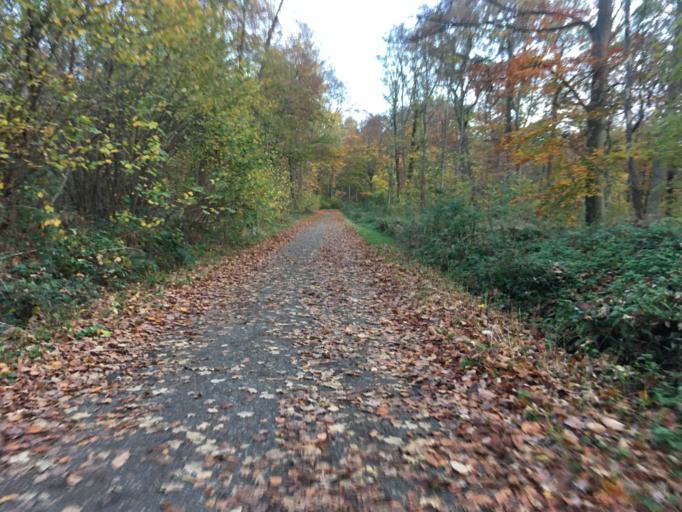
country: DE
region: Baden-Wuerttemberg
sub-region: Regierungsbezirk Stuttgart
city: Weinsberg
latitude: 49.1449
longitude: 9.2657
